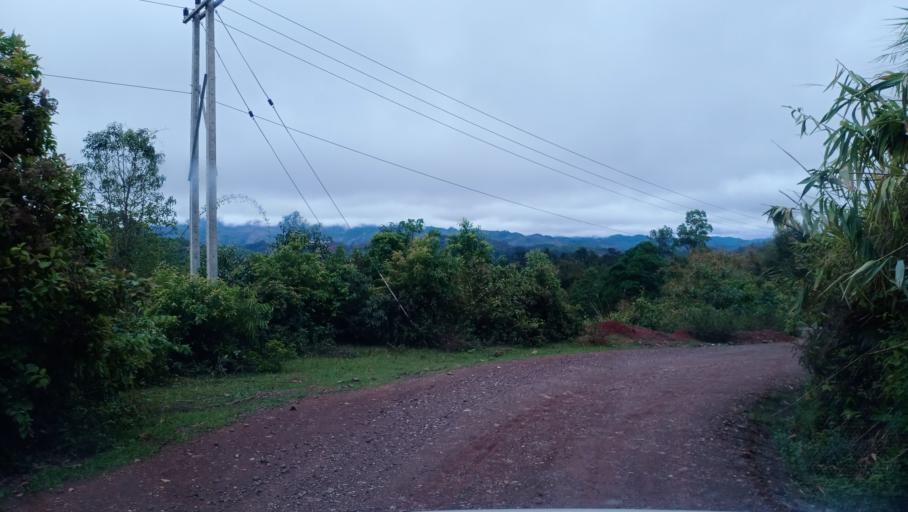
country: LA
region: Phongsali
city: Phongsali
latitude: 21.3414
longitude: 102.0763
